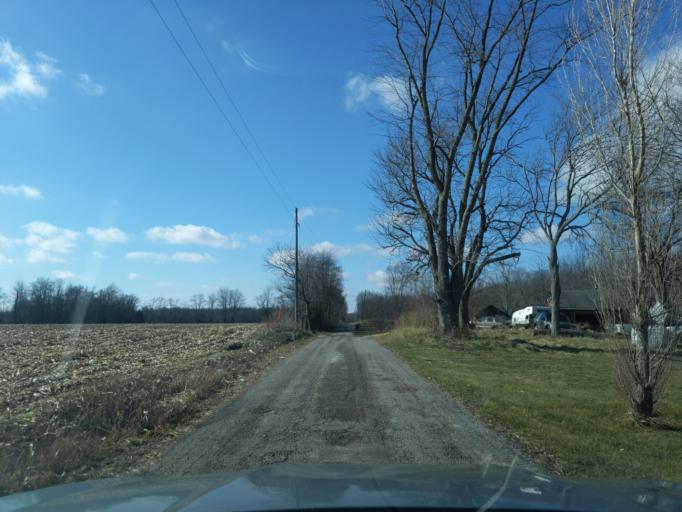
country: US
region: Indiana
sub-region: Decatur County
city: Greensburg
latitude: 39.2409
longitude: -85.4497
